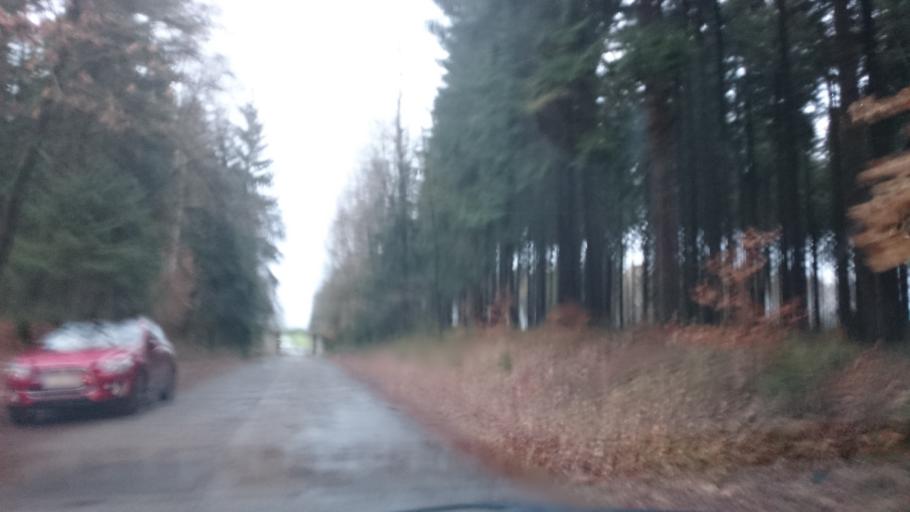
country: DE
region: Saxony
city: Hirschfeld
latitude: 50.6476
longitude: 12.4724
